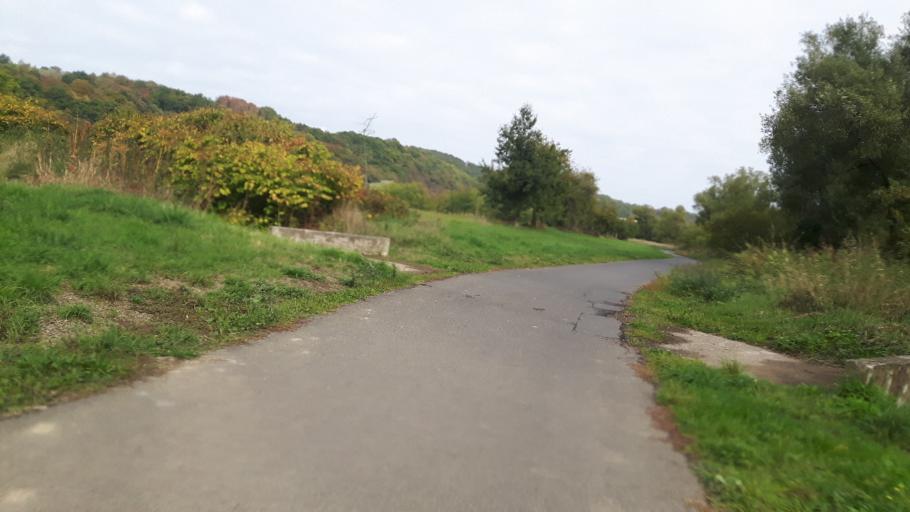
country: DE
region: North Rhine-Westphalia
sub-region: Regierungsbezirk Koln
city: Eitorf
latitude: 50.7761
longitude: 7.4203
